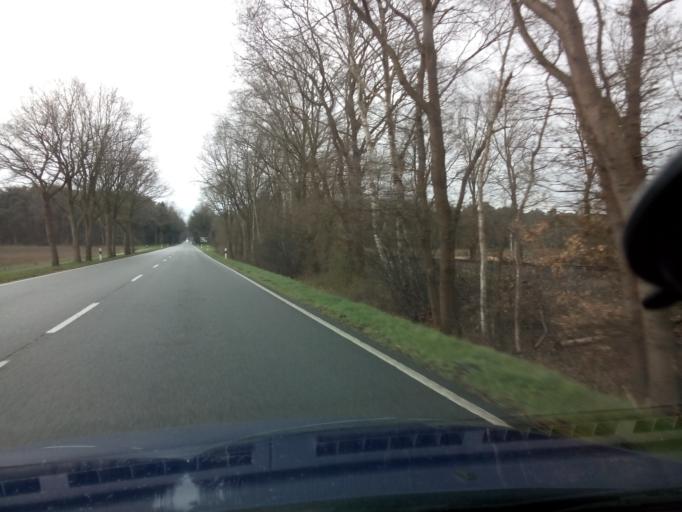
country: DE
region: Lower Saxony
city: Herzlake
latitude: 52.7067
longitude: 7.6314
